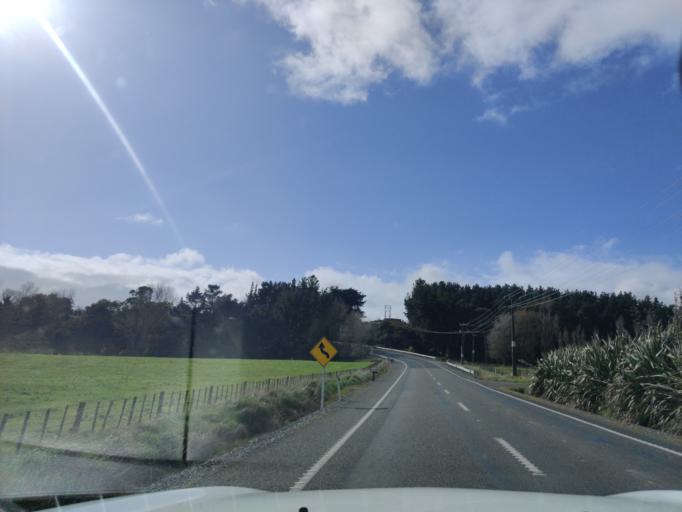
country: NZ
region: Manawatu-Wanganui
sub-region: Palmerston North City
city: Palmerston North
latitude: -40.4039
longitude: 175.6177
